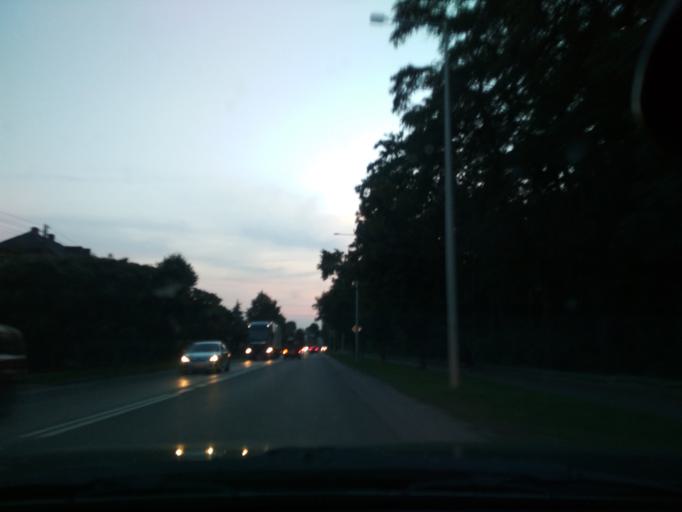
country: PL
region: Silesian Voivodeship
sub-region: Powiat zawiercianski
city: Zawiercie
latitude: 50.4784
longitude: 19.4500
